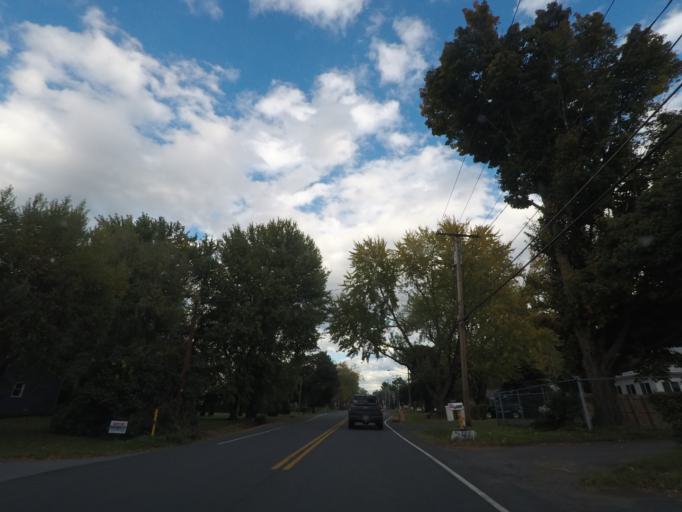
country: US
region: New York
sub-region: Rensselaer County
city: Rensselaer
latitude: 42.6371
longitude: -73.7306
